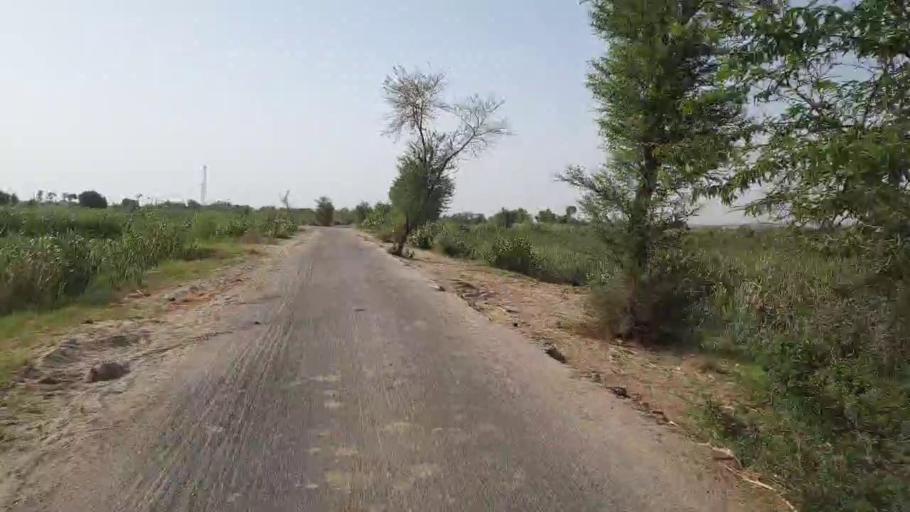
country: PK
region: Sindh
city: Kandiari
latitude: 26.7038
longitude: 68.9643
